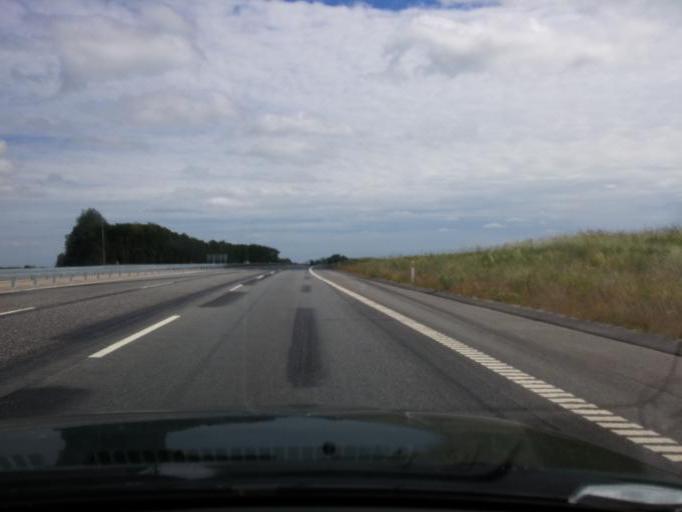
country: DK
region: South Denmark
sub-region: Middelfart Kommune
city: Strib
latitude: 55.5119
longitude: 9.7767
